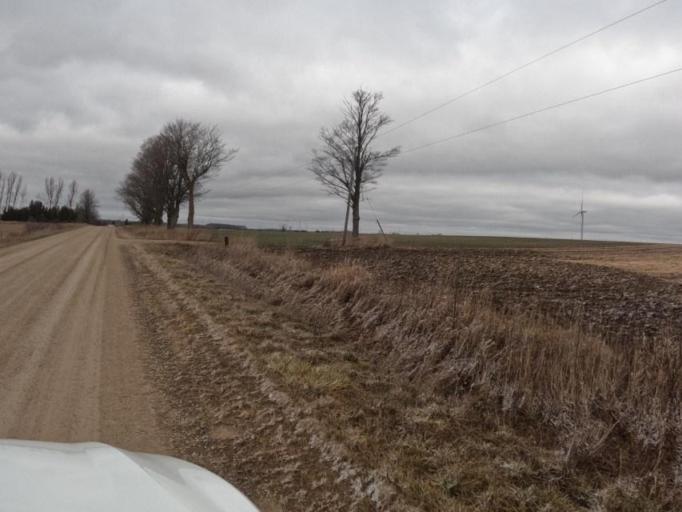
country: CA
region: Ontario
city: Shelburne
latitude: 44.0293
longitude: -80.3709
